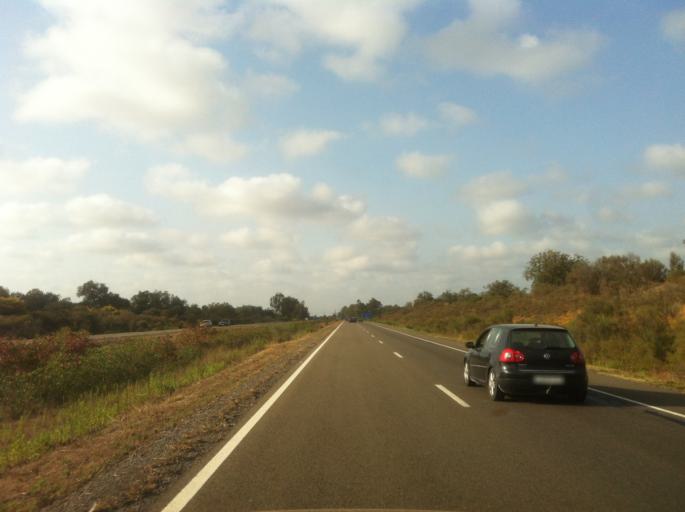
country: MA
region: Gharb-Chrarda-Beni Hssen
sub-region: Kenitra Province
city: Kenitra
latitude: 34.2245
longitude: -6.5477
